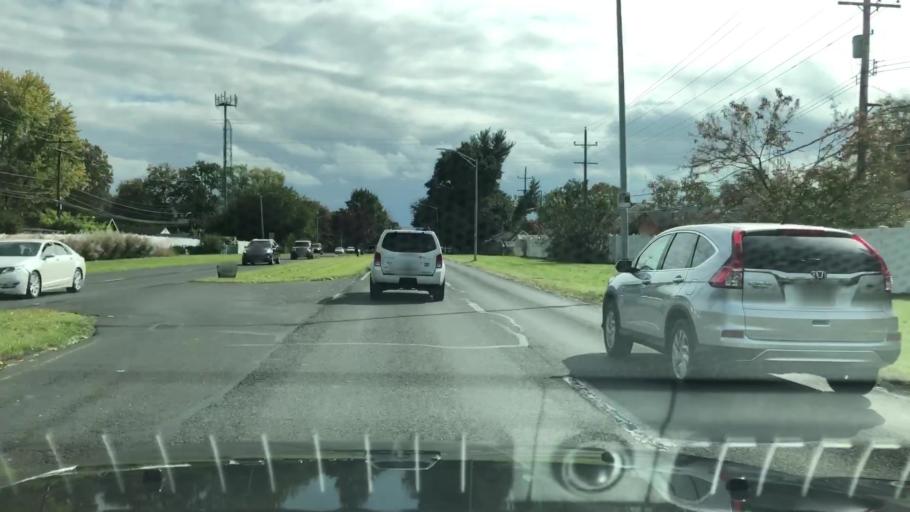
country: US
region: Pennsylvania
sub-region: Bucks County
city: Levittown
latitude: 40.1601
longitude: -74.8321
